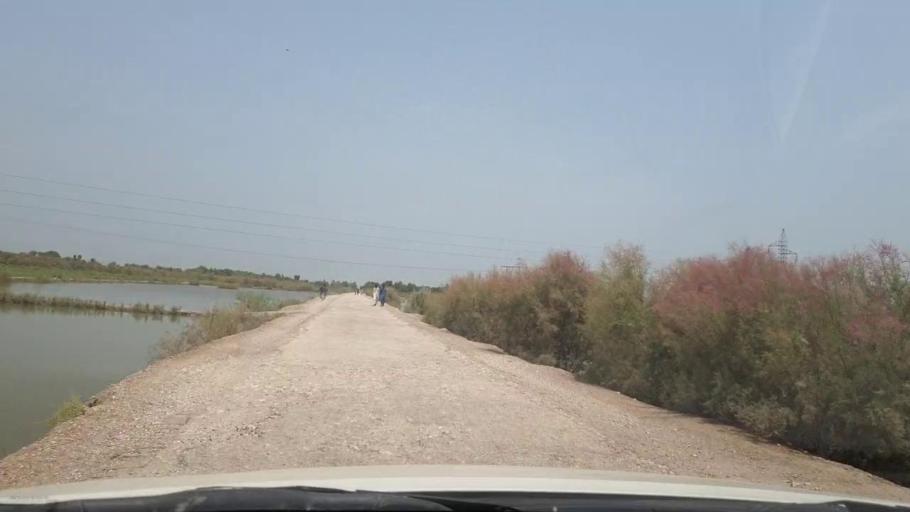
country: PK
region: Sindh
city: Rustam jo Goth
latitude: 28.0259
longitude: 68.8129
